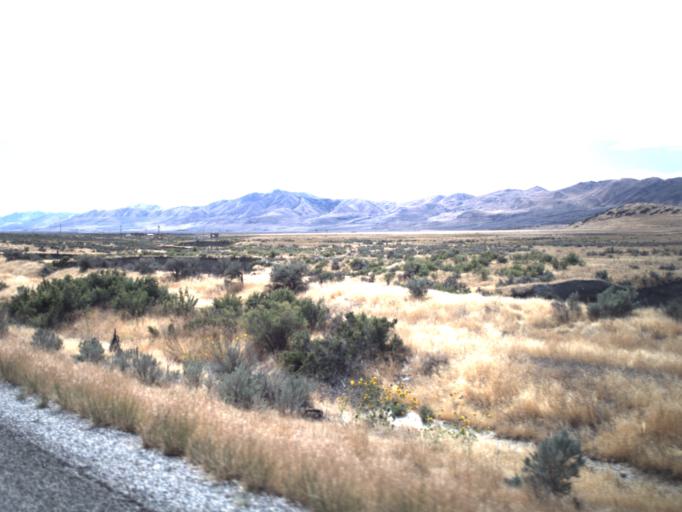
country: US
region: Utah
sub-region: Box Elder County
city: Tremonton
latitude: 41.6676
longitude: -112.4457
